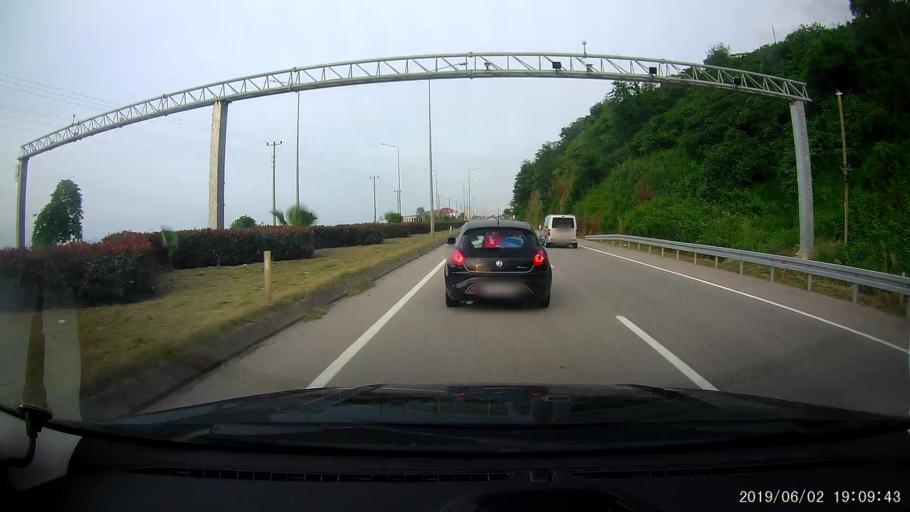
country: TR
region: Ordu
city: Gulyali
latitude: 40.9723
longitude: 38.0330
